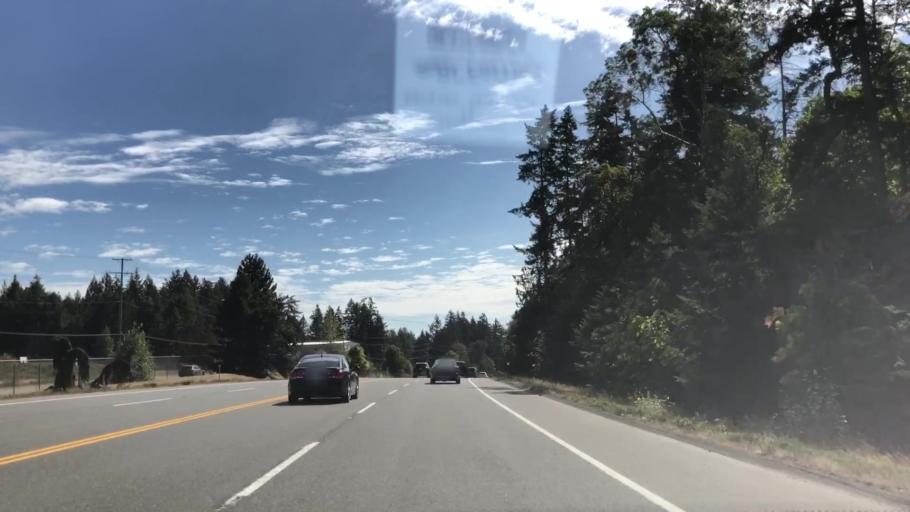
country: CA
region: British Columbia
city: Nanaimo
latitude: 49.1340
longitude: -123.8700
